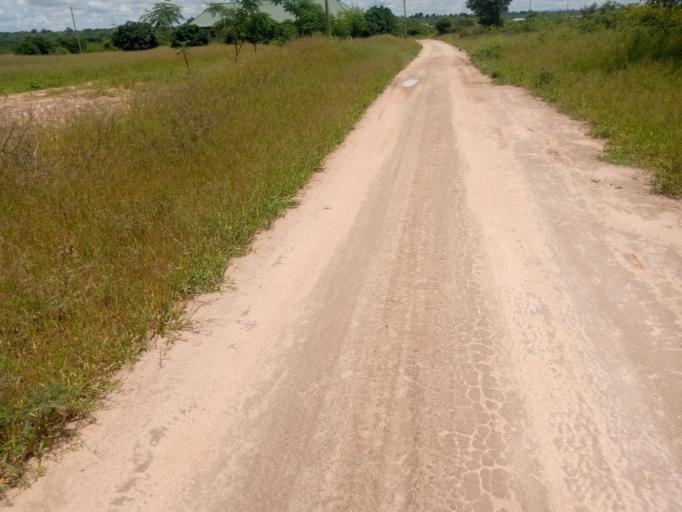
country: TZ
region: Dodoma
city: Dodoma
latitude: -6.1137
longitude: 35.7393
